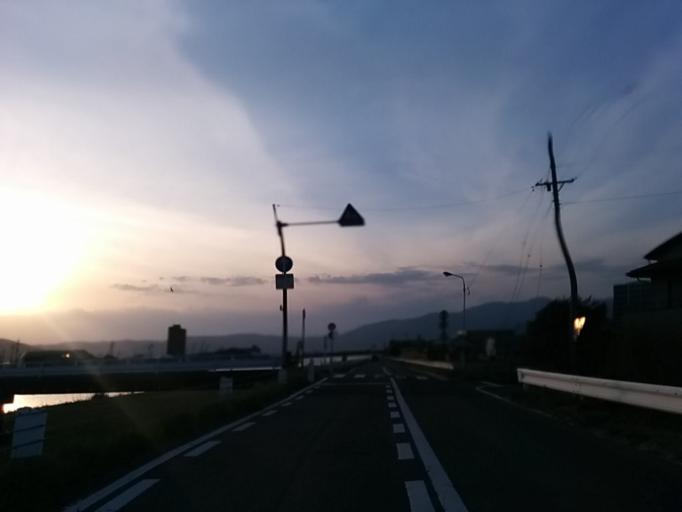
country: JP
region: Nagano
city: Suwa
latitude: 36.0356
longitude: 138.1048
